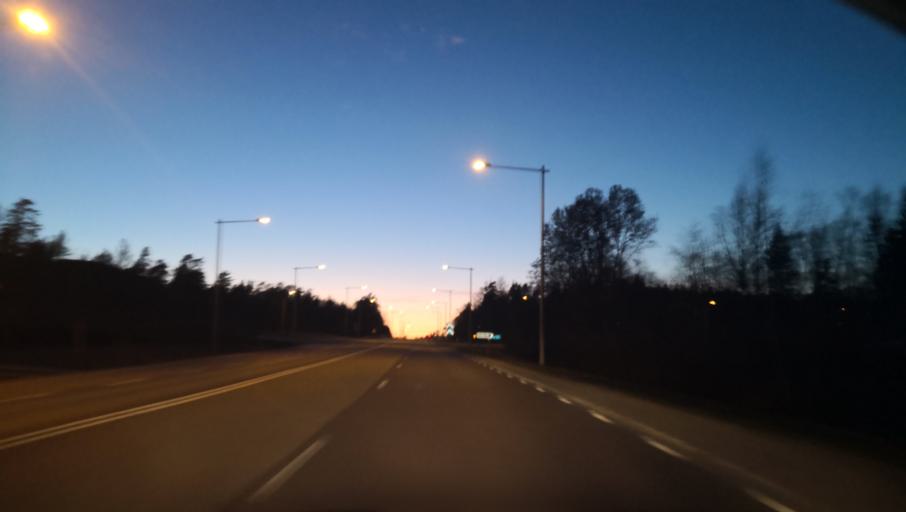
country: SE
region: Stockholm
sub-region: Nynashamns Kommun
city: Nynashamn
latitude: 58.9188
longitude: 17.9546
